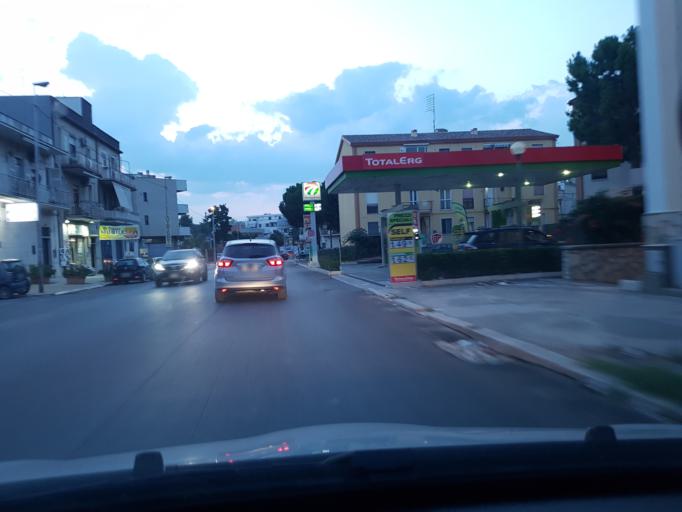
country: IT
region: Apulia
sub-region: Provincia di Foggia
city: Cerignola
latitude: 41.2617
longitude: 15.8899
